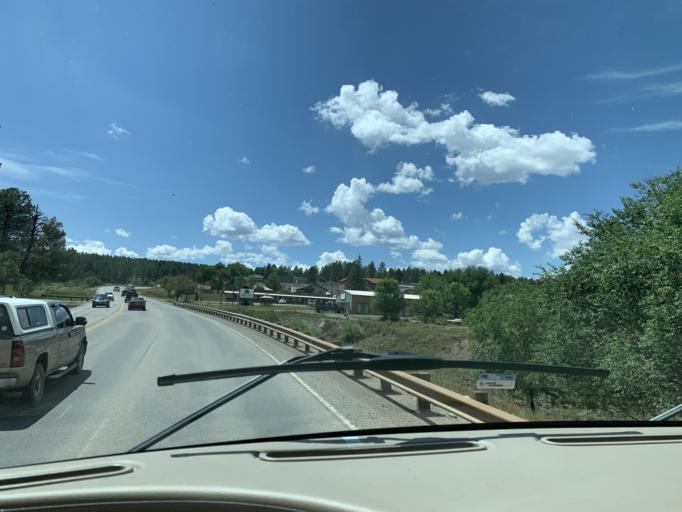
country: US
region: Colorado
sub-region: Archuleta County
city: Pagosa Springs
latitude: 37.2672
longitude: -107.0218
